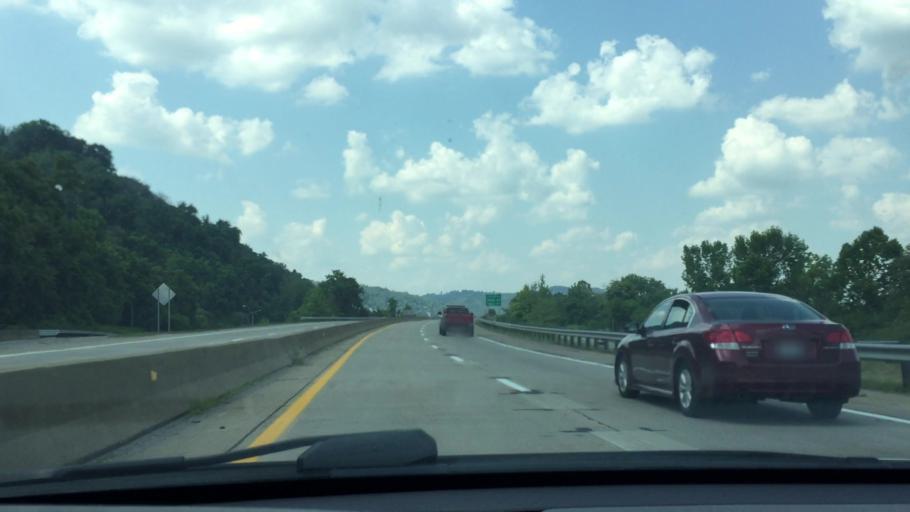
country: US
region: West Virginia
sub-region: Marshall County
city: McMechen
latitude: 39.9925
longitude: -80.7414
